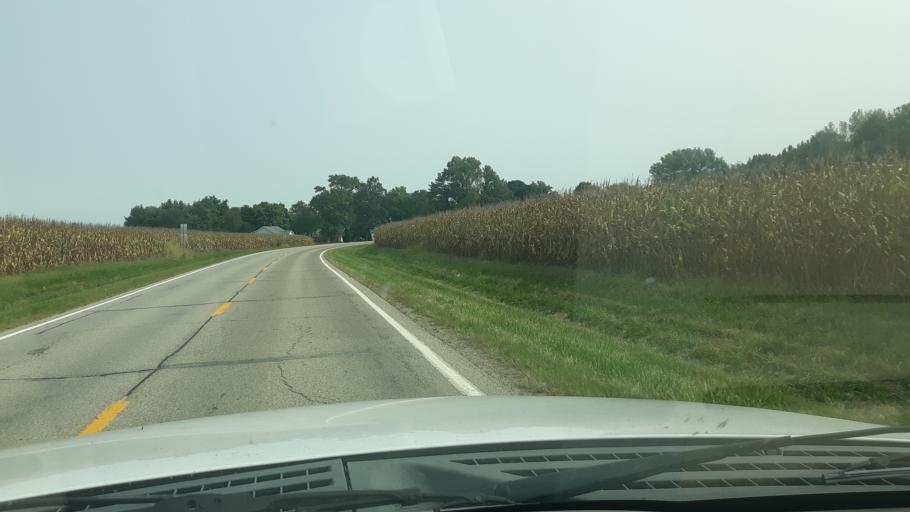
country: US
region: Illinois
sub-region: Edwards County
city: Grayville
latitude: 38.3092
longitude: -87.9425
